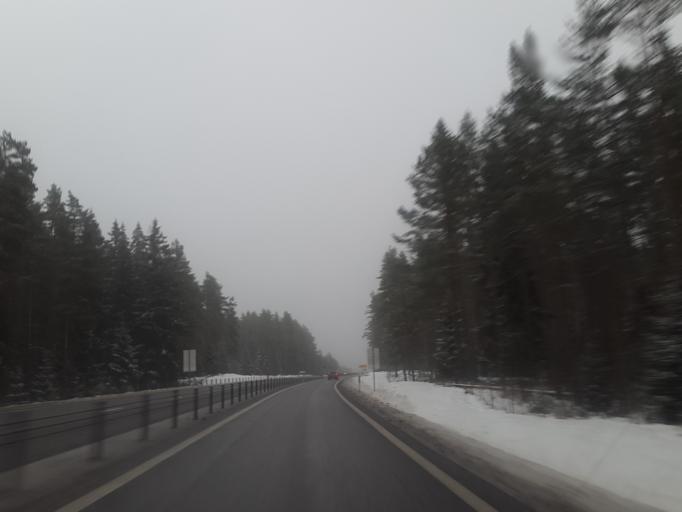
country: SE
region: Joenkoeping
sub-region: Mullsjo Kommun
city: Mullsjoe
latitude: 57.7688
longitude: 13.8073
